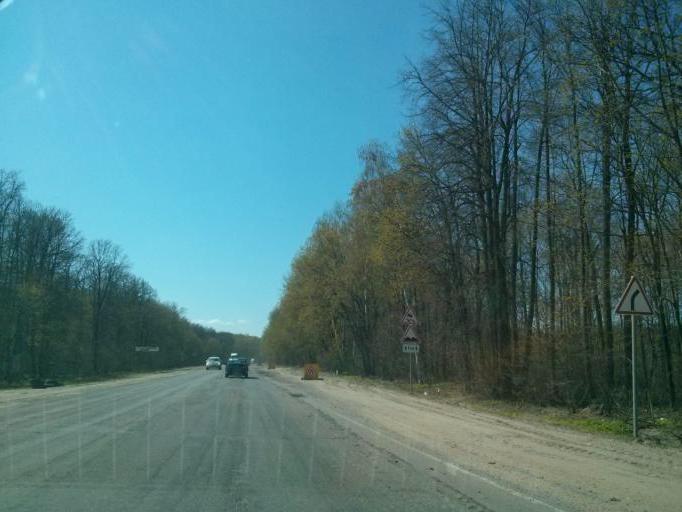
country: RU
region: Nizjnij Novgorod
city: Afonino
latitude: 56.2120
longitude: 44.0208
